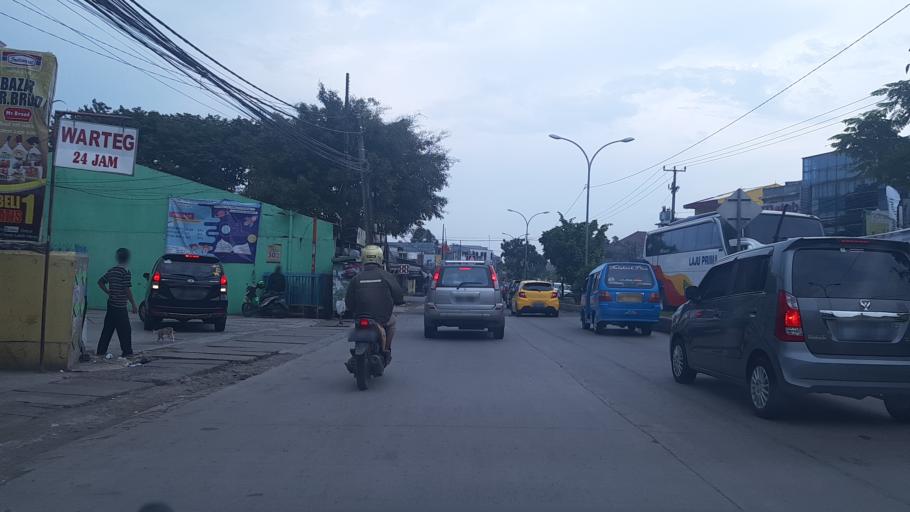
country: ID
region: West Java
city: Cibinong
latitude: -6.4700
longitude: 106.8609
